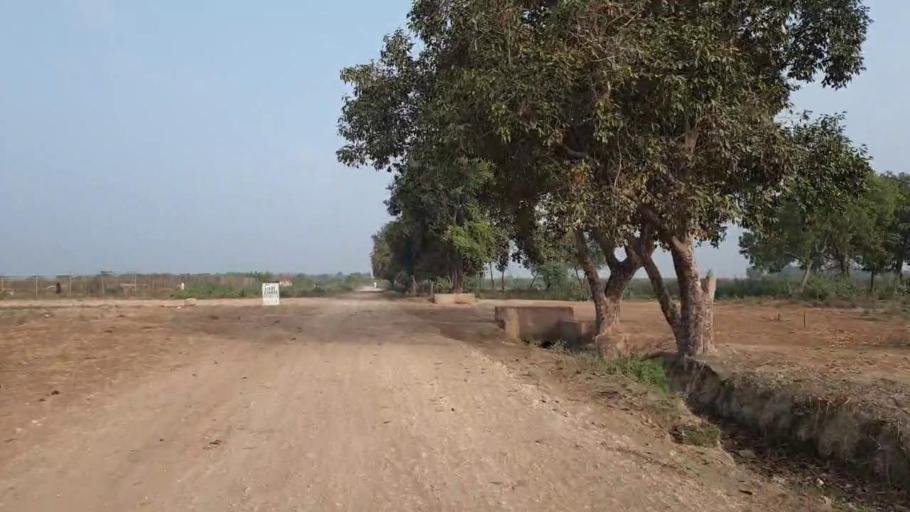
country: PK
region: Sindh
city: Tando Muhammad Khan
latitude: 25.1409
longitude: 68.5918
